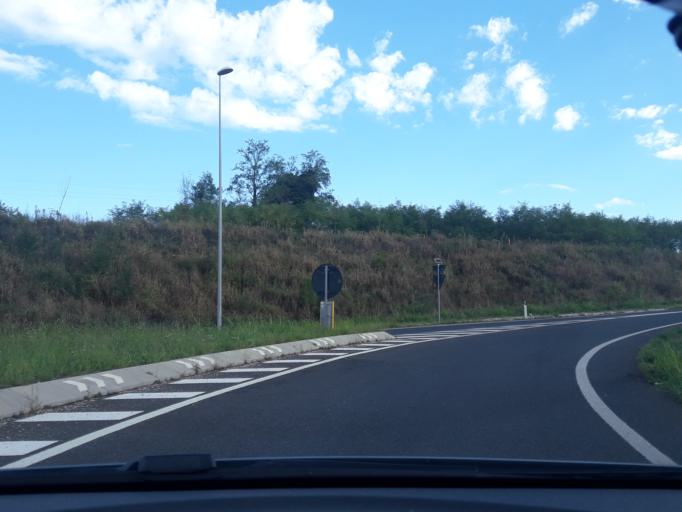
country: IT
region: Friuli Venezia Giulia
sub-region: Provincia di Udine
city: Pasian di Prato
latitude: 46.0404
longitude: 13.1869
